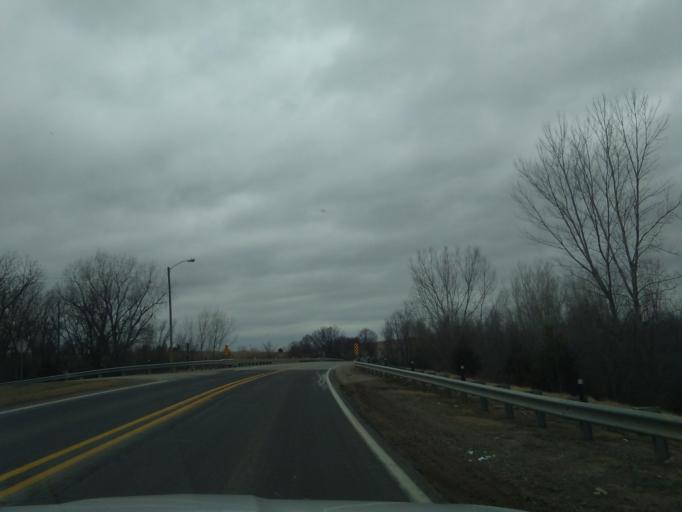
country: US
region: Nebraska
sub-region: Richardson County
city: Falls City
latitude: 40.0538
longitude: -95.4341
